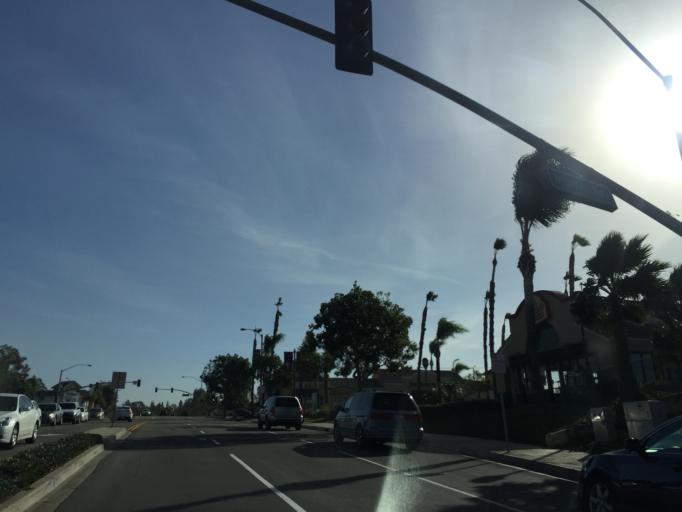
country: US
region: California
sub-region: Orange County
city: Yorba Linda
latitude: 33.8885
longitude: -117.8130
